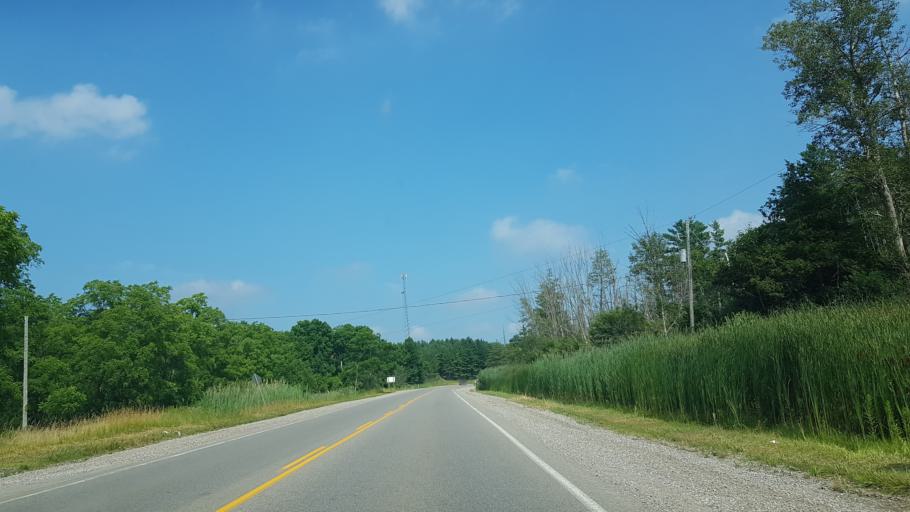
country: CA
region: Ontario
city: Delaware
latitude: 42.9650
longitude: -81.3806
